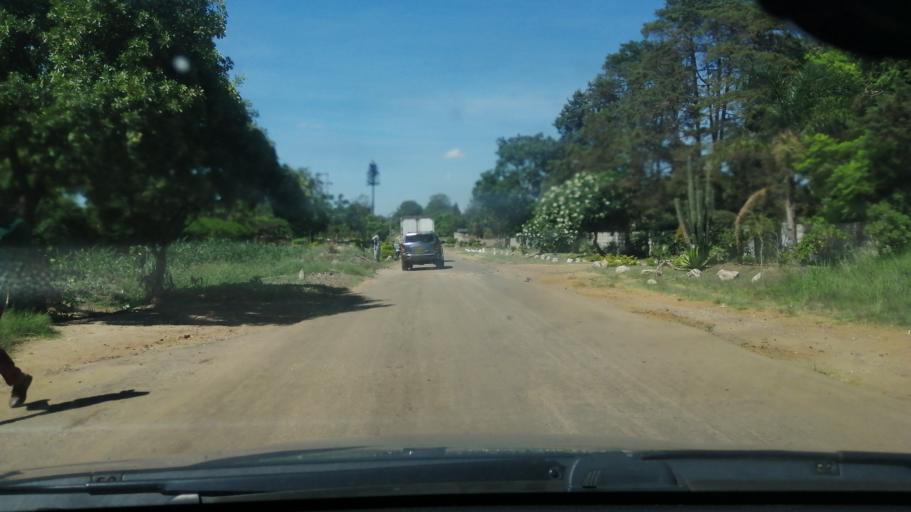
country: ZW
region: Harare
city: Epworth
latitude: -17.8199
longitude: 31.1299
